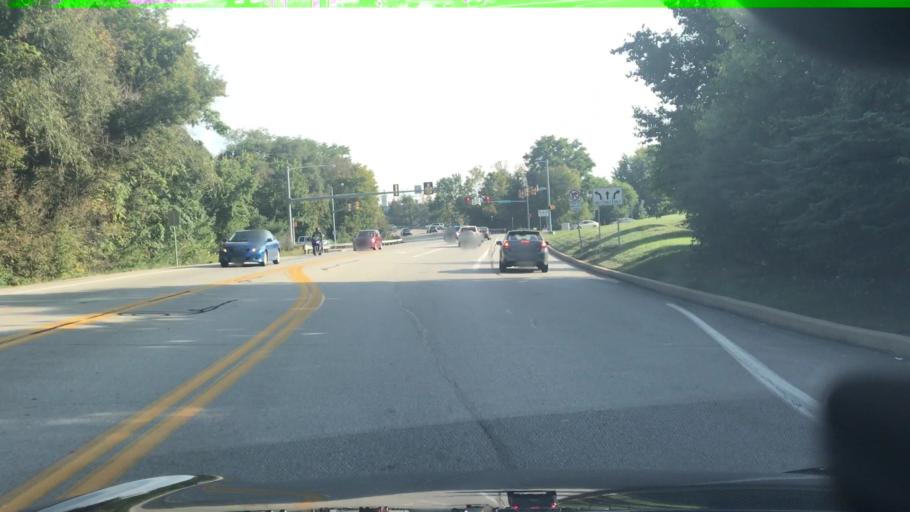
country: US
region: Pennsylvania
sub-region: Cumberland County
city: Shiremanstown
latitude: 40.2129
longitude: -76.9451
